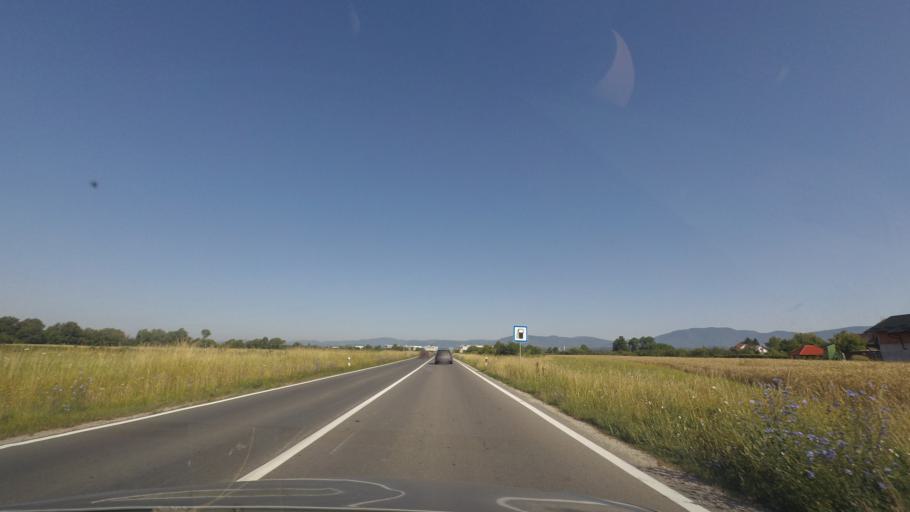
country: HR
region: Zagrebacka
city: Jastrebarsko
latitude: 45.6470
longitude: 15.6712
